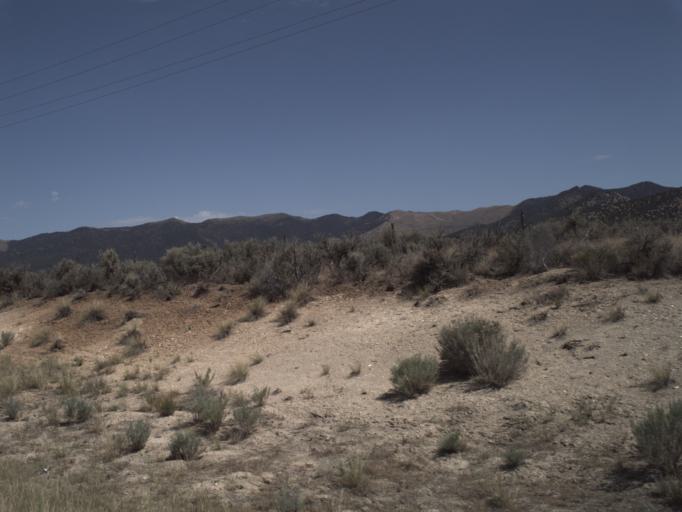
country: US
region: Utah
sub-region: Juab County
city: Mona
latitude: 39.9249
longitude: -112.1559
